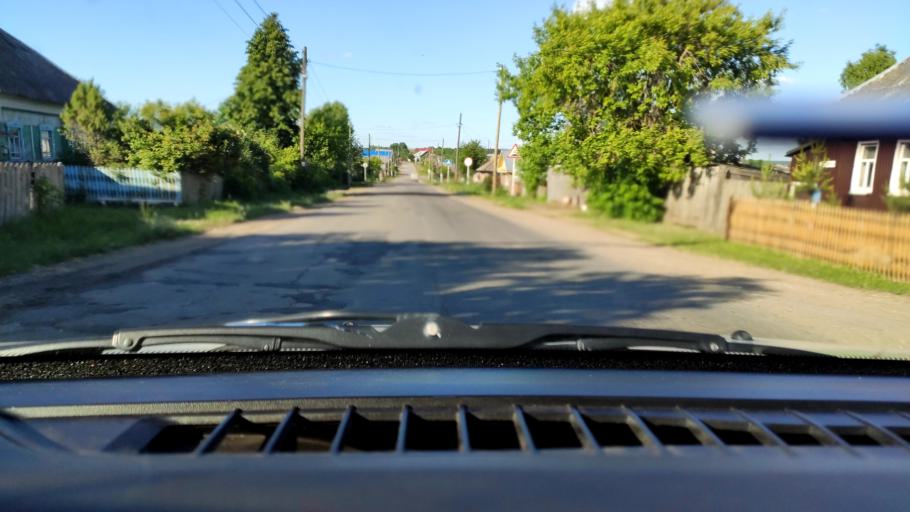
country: RU
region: Perm
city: Orda
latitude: 57.1908
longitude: 56.8909
